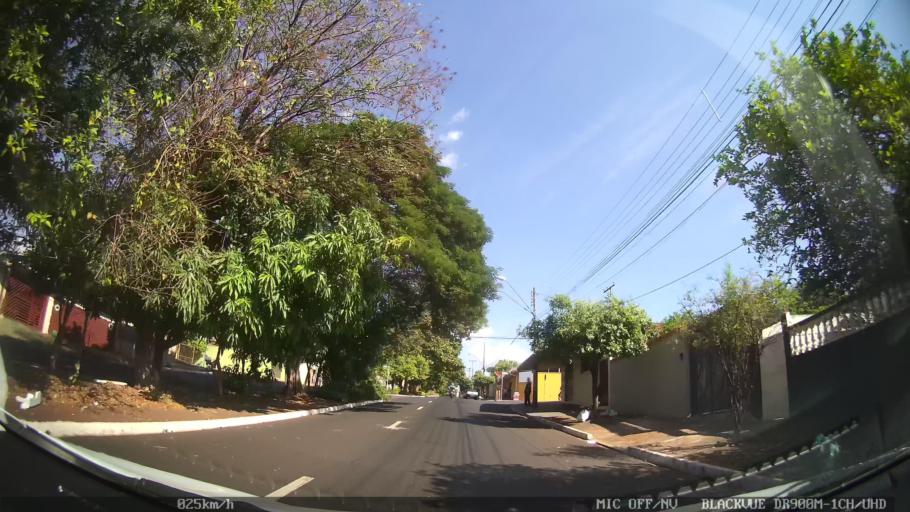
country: BR
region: Sao Paulo
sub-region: Ribeirao Preto
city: Ribeirao Preto
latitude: -21.1798
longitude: -47.8314
